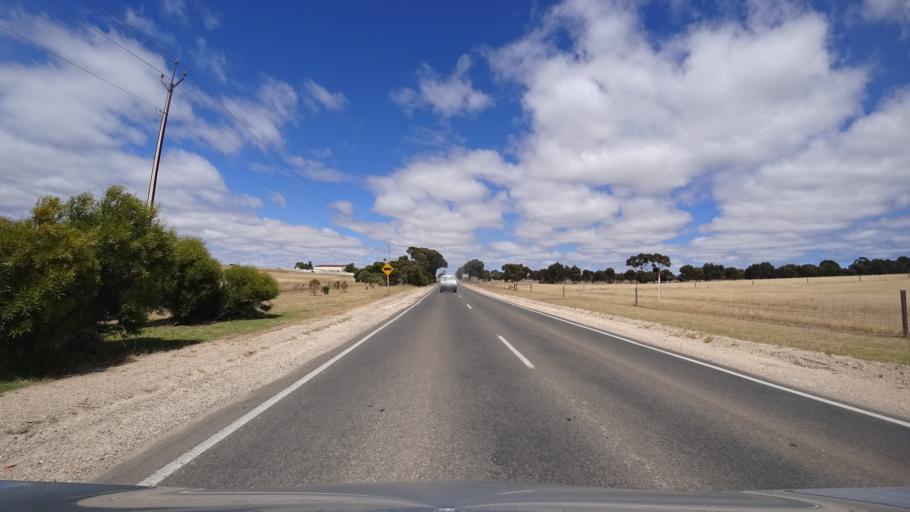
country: AU
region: South Australia
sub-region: Kangaroo Island
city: Kingscote
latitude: -35.6531
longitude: 137.6255
